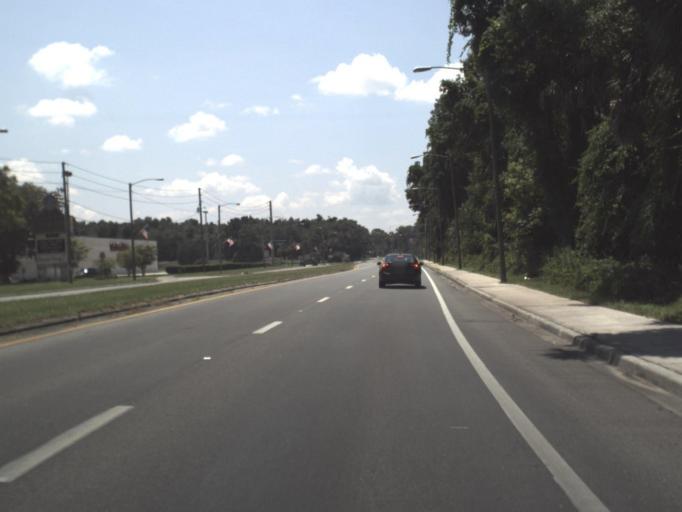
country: US
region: Florida
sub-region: Citrus County
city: Crystal River
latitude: 28.9090
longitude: -82.6051
